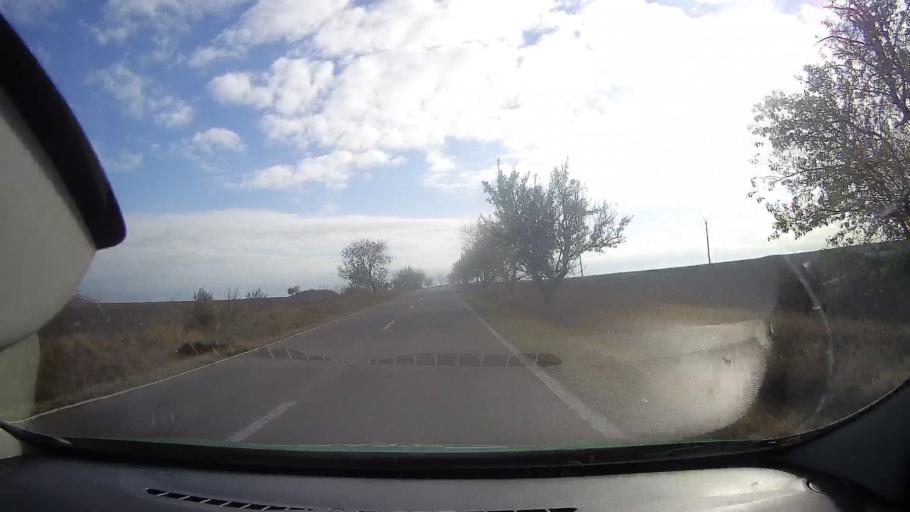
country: RO
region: Tulcea
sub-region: Comuna Bestepe
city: Bestepe
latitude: 45.0788
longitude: 29.0410
